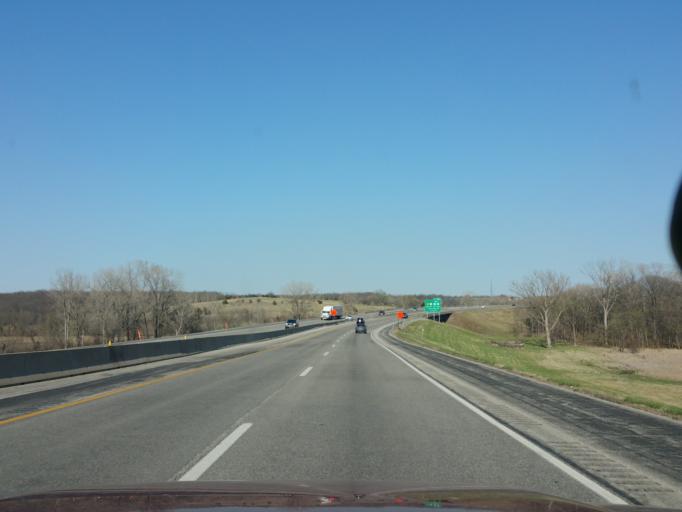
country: US
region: Kansas
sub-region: Wyandotte County
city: Bonner Springs
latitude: 39.0876
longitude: -94.9224
